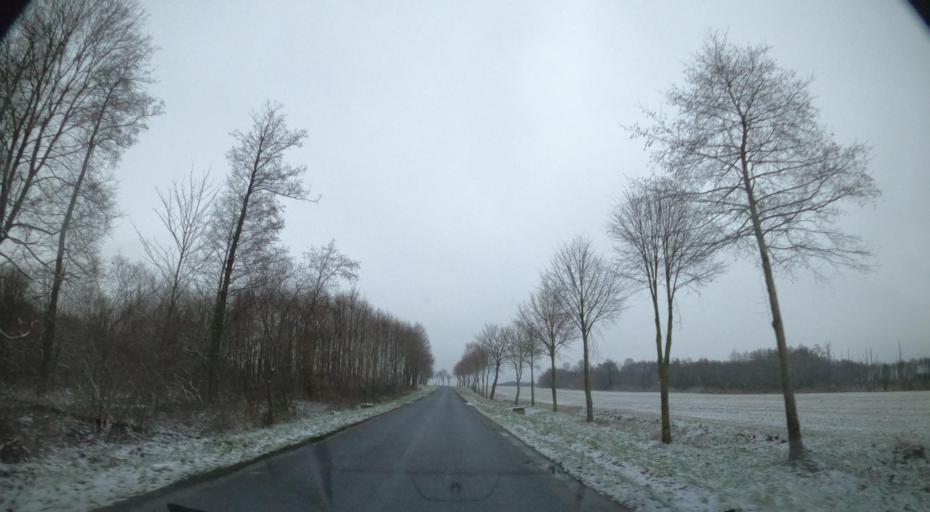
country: PL
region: Kujawsko-Pomorskie
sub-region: Powiat lipnowski
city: Wielgie
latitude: 52.7015
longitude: 19.2862
